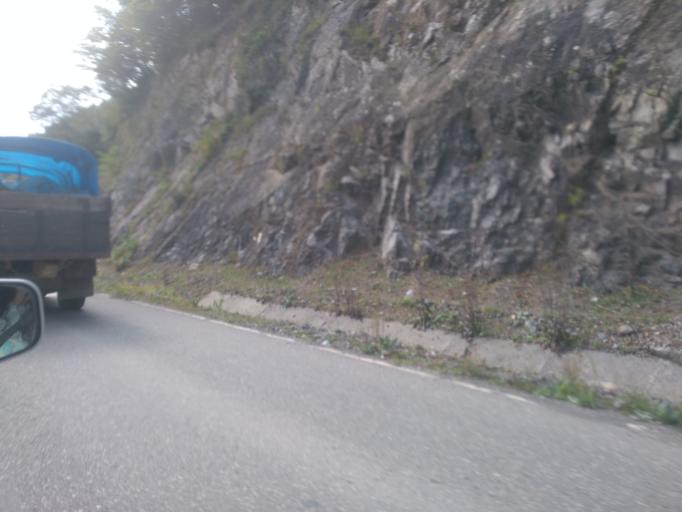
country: TR
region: Artvin
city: Muratli
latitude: 41.5528
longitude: 41.8021
